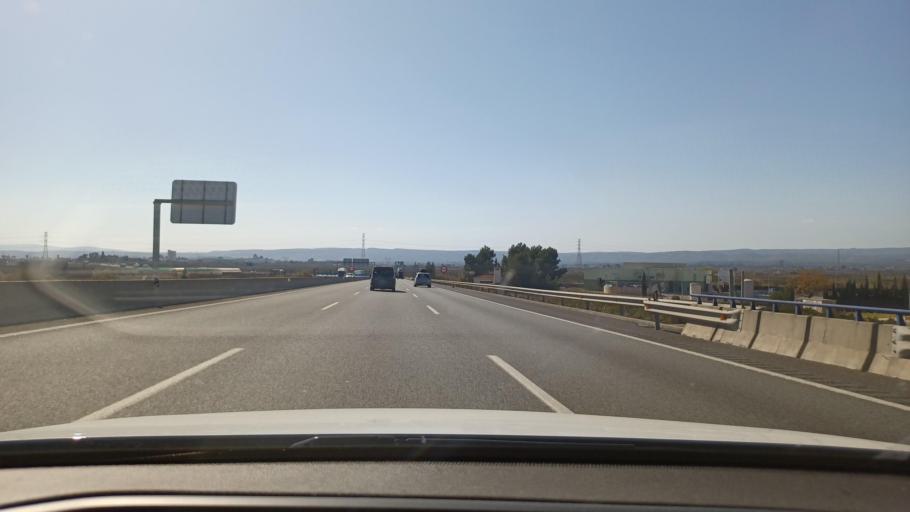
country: ES
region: Valencia
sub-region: Provincia de Valencia
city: L'Alcudia
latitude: 39.1851
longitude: -0.5088
